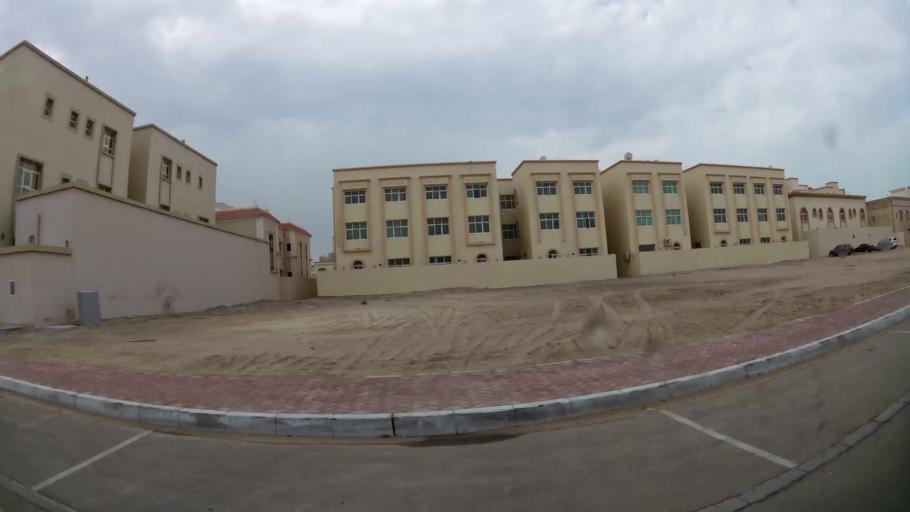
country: AE
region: Abu Dhabi
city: Abu Dhabi
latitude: 24.4317
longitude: 54.4456
